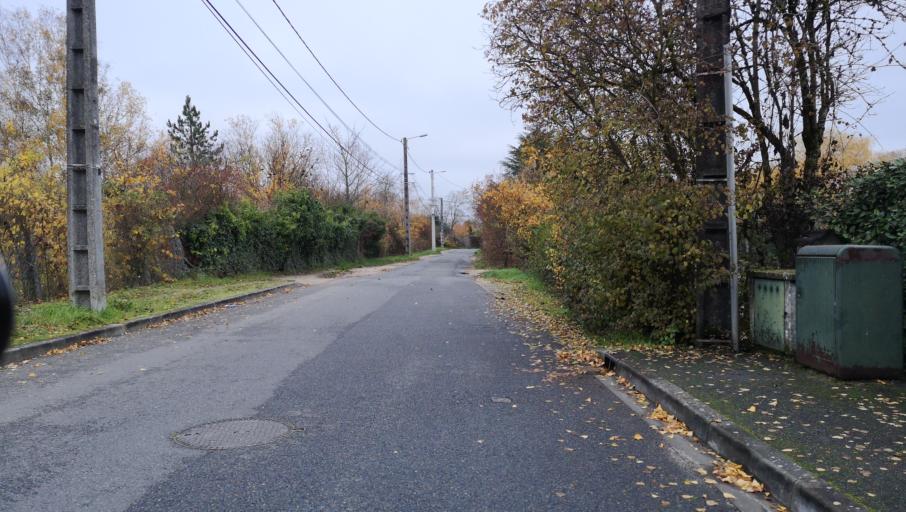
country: FR
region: Centre
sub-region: Departement du Loiret
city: Fleury-les-Aubrais
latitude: 47.9220
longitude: 1.9328
